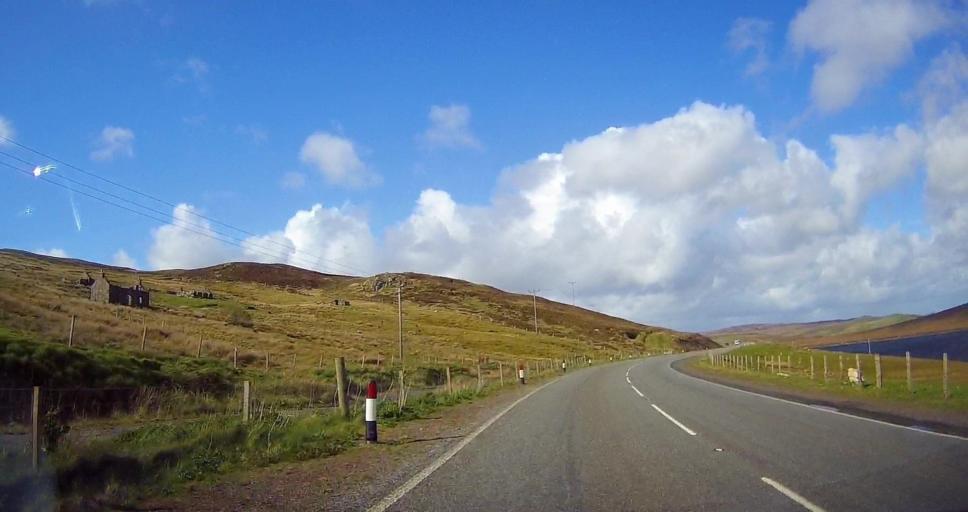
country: GB
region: Scotland
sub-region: Shetland Islands
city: Lerwick
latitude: 60.2555
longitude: -1.2268
